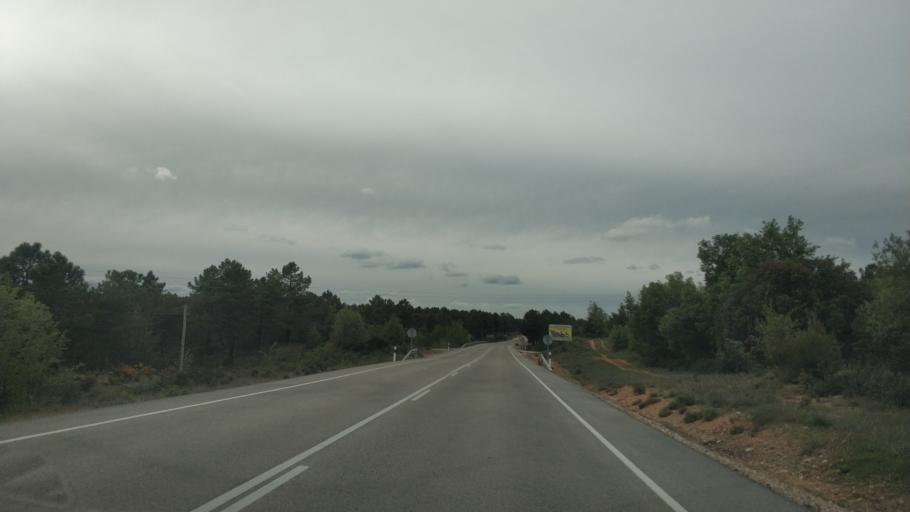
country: ES
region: Castille and Leon
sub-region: Provincia de Soria
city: Quintanas de Gormaz
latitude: 41.5363
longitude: -2.9515
